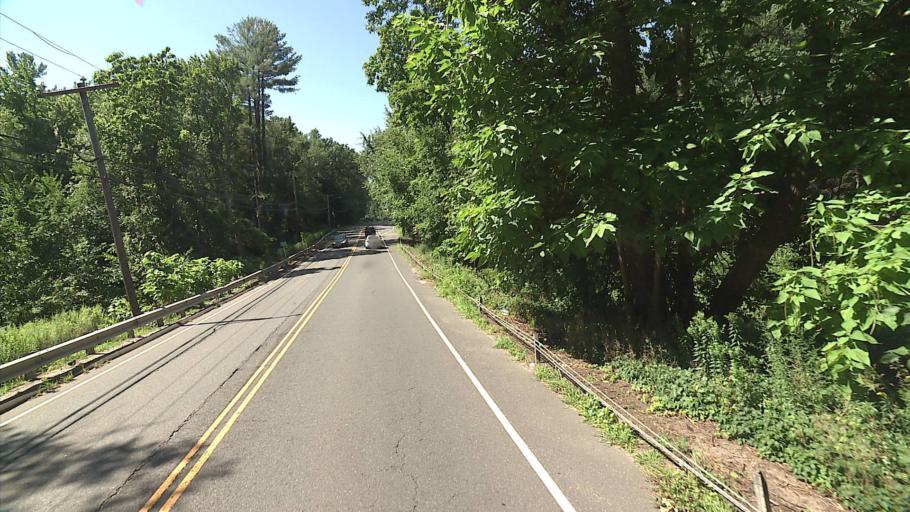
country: US
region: Connecticut
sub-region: Hartford County
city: Weatogue
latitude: 41.8562
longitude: -72.8116
